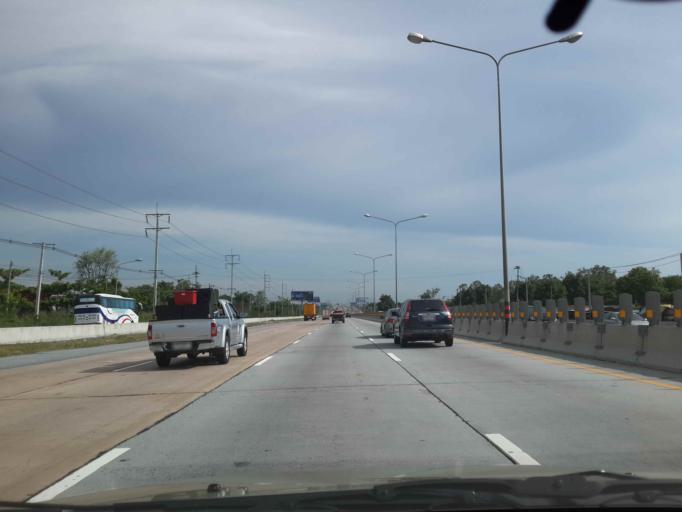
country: TH
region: Chon Buri
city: Si Racha
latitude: 13.1904
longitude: 100.9986
